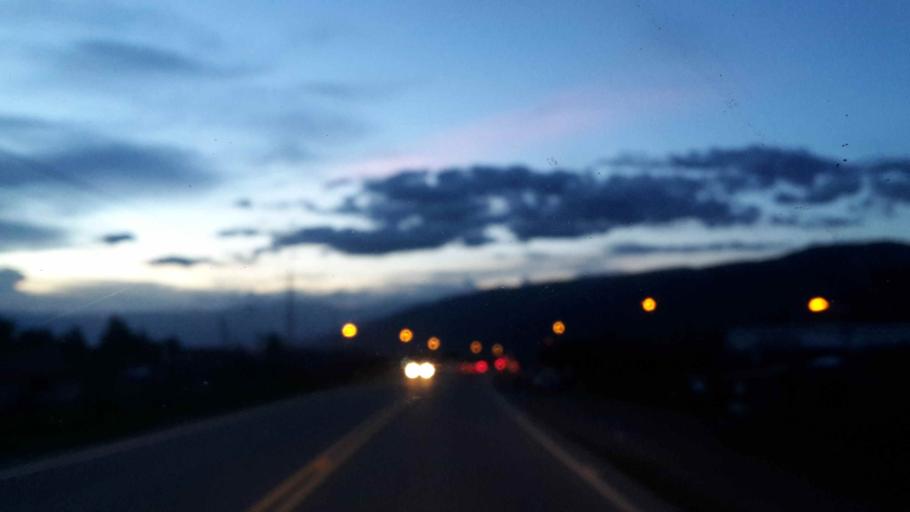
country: BO
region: Cochabamba
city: Colomi
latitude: -17.4185
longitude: -65.9558
